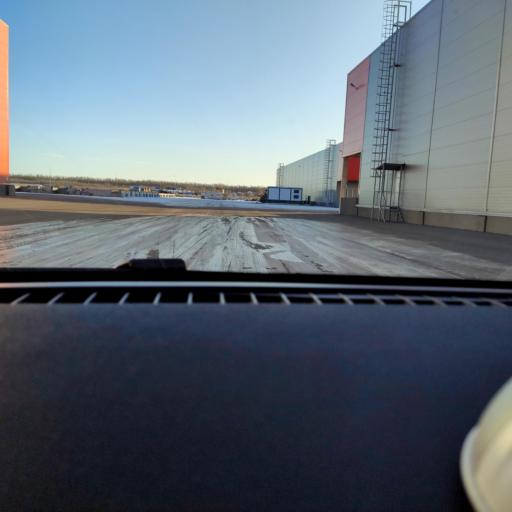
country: RU
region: Samara
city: Samara
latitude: 53.0918
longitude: 50.1287
